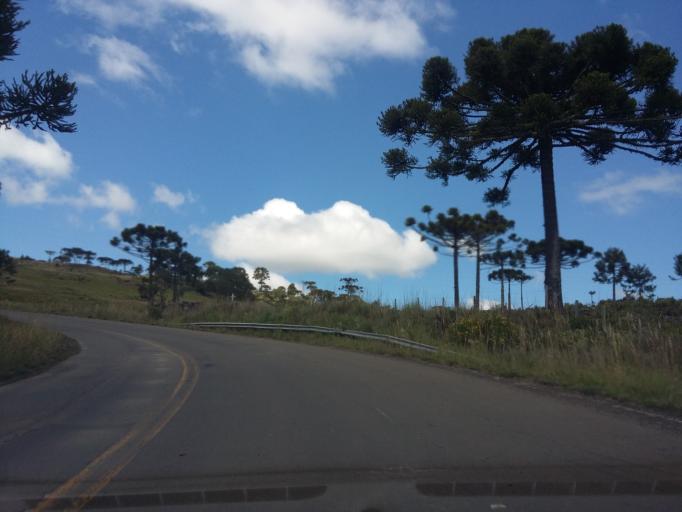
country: BR
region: Santa Catarina
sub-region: Sao Joaquim
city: Sao Joaquim
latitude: -28.2701
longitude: -49.7613
